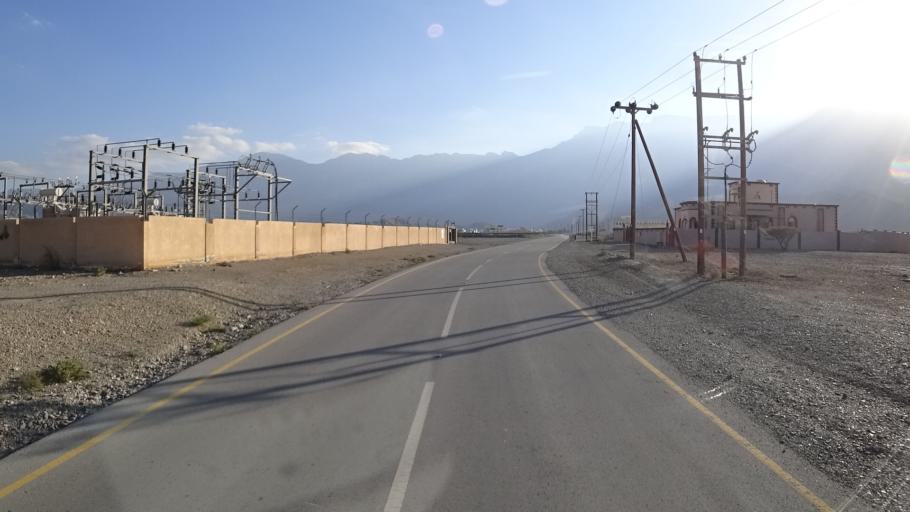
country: OM
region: Al Batinah
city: Rustaq
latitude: 23.2822
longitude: 57.3291
